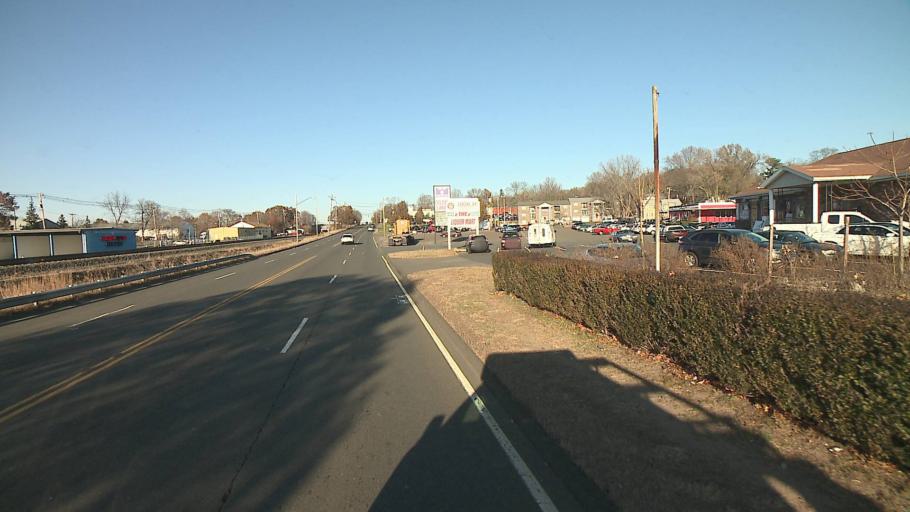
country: US
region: Connecticut
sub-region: New Haven County
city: Wallingford Center
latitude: 41.4423
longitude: -72.8312
